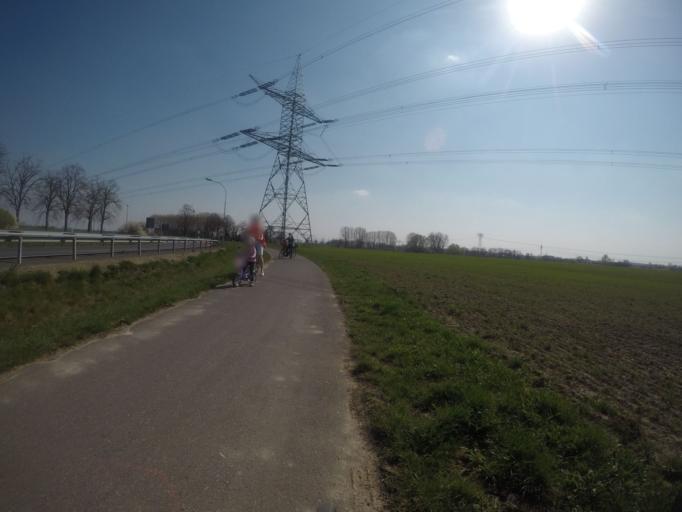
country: DE
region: Brandenburg
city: Nauen
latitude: 52.5930
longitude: 12.8729
